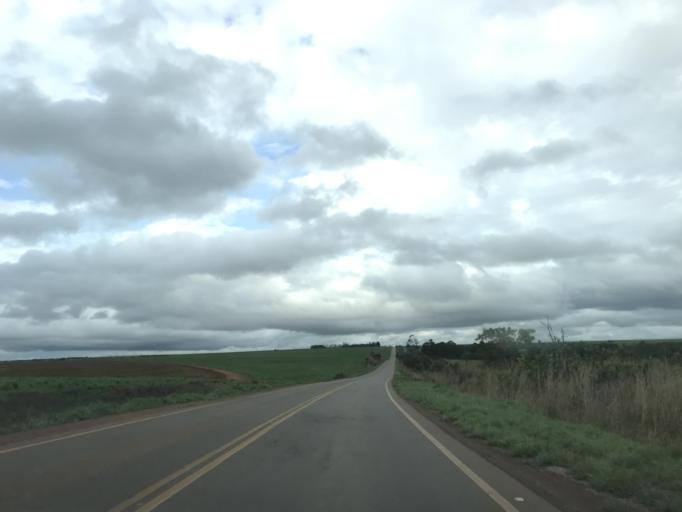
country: BR
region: Goias
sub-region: Vianopolis
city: Vianopolis
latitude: -16.5654
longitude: -48.2897
